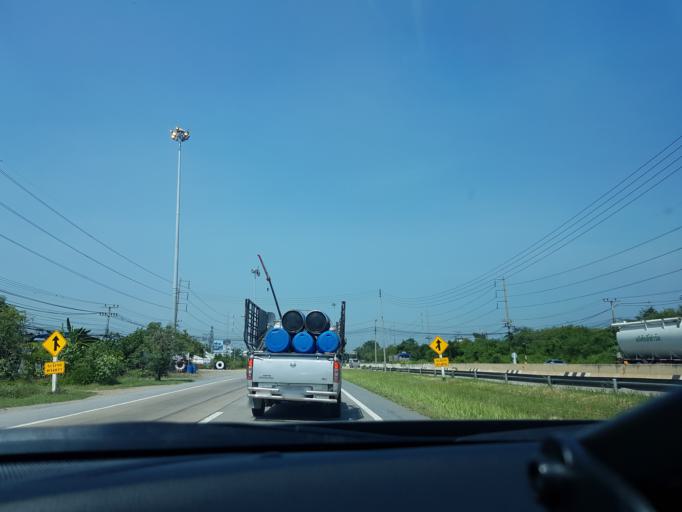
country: TH
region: Sara Buri
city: Saraburi
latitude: 14.5026
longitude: 100.9150
